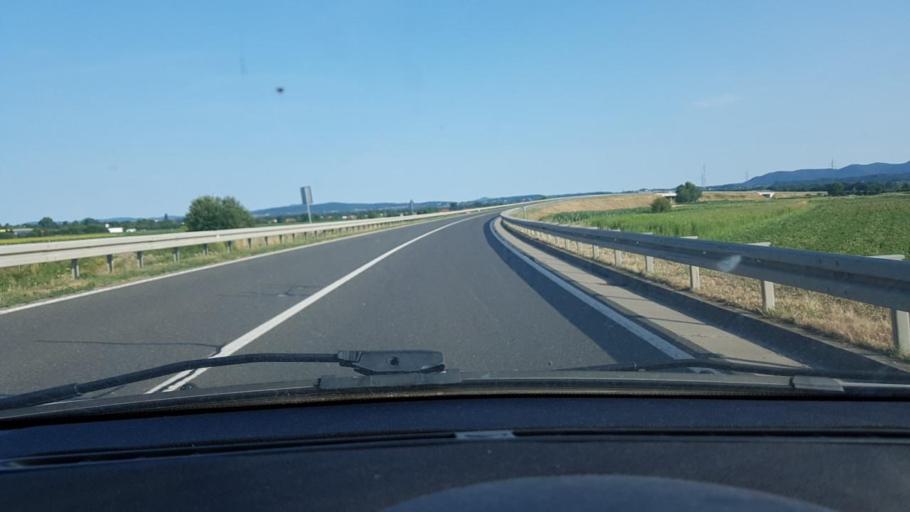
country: HR
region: Varazdinska
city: Jalkovec
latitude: 46.2900
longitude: 16.3103
